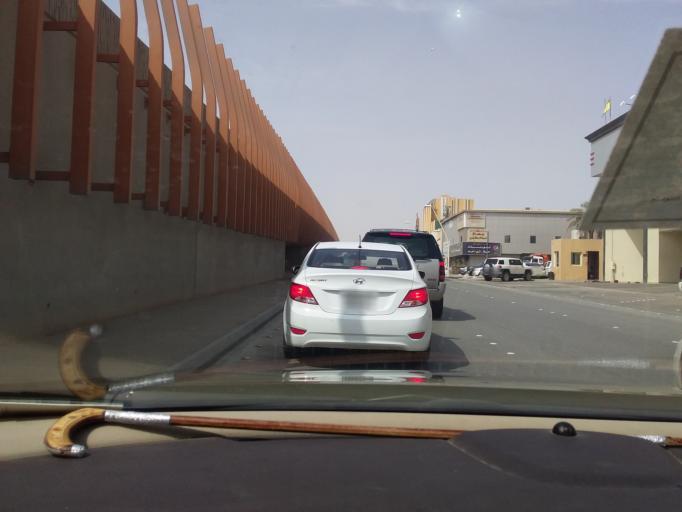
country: SA
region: Ar Riyad
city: Riyadh
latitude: 24.7418
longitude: 46.7045
